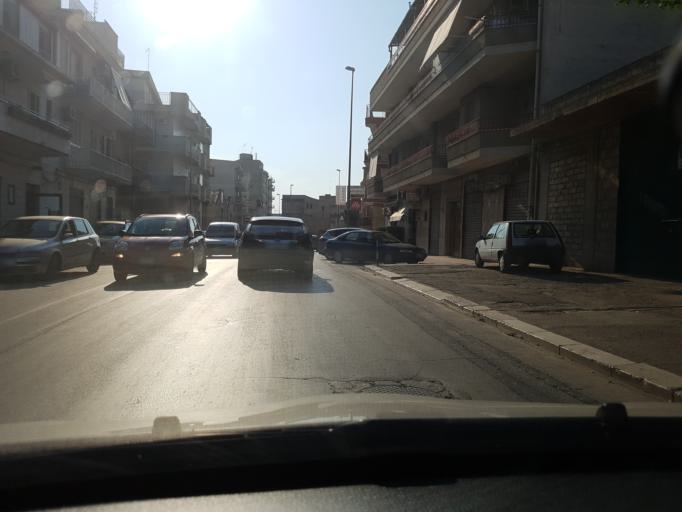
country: IT
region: Apulia
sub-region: Provincia di Foggia
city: Cerignola
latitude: 41.2686
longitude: 15.9024
